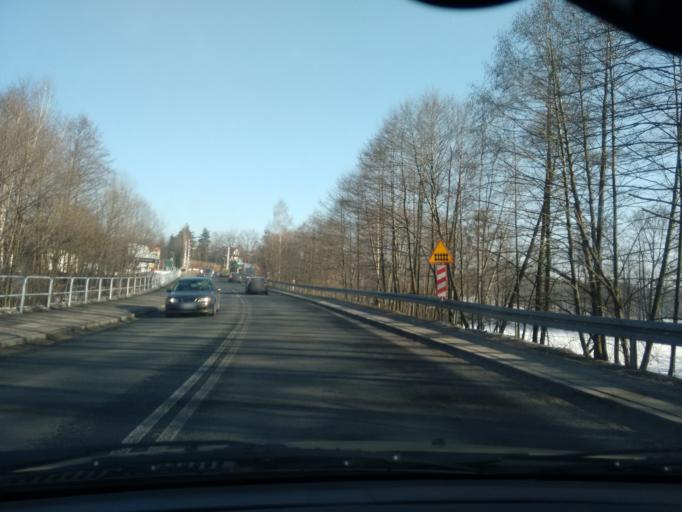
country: PL
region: Lesser Poland Voivodeship
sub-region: Powiat oswiecimski
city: Bulowice
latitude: 49.8755
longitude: 19.2885
